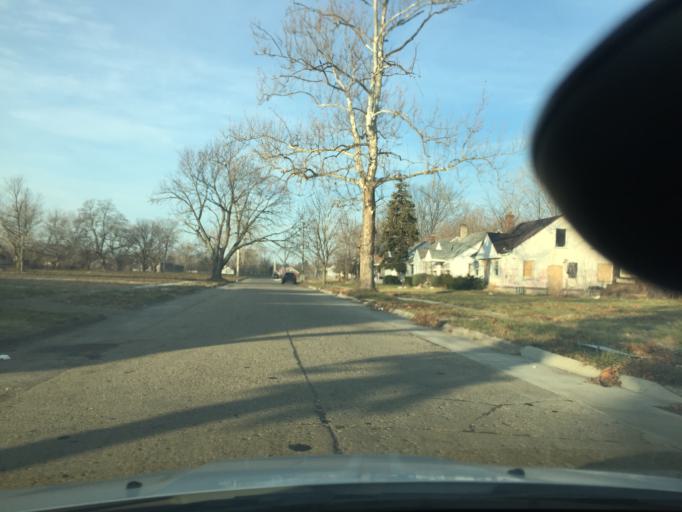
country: US
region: Michigan
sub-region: Macomb County
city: Eastpointe
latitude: 42.4392
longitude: -82.9585
